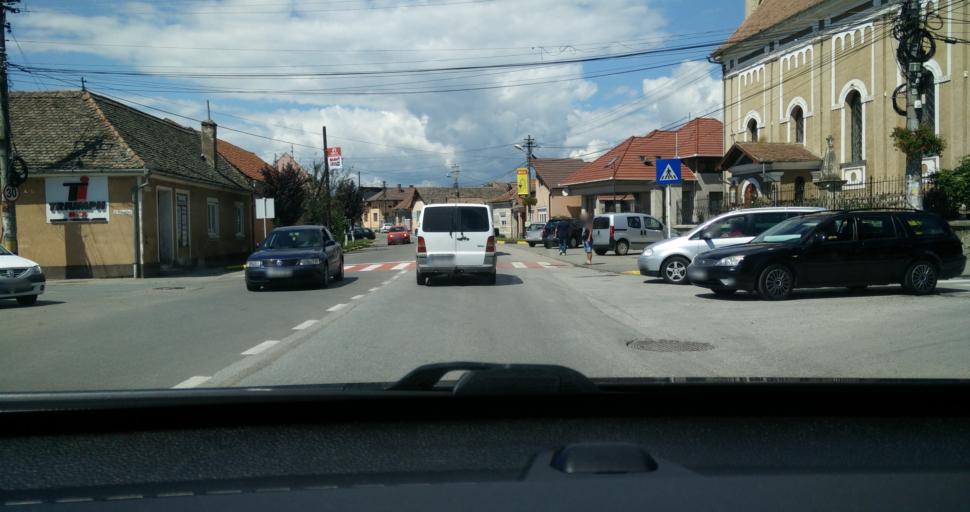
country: RO
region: Alba
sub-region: Municipiul Sebes
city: Sebes
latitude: 45.9587
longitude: 23.5613
